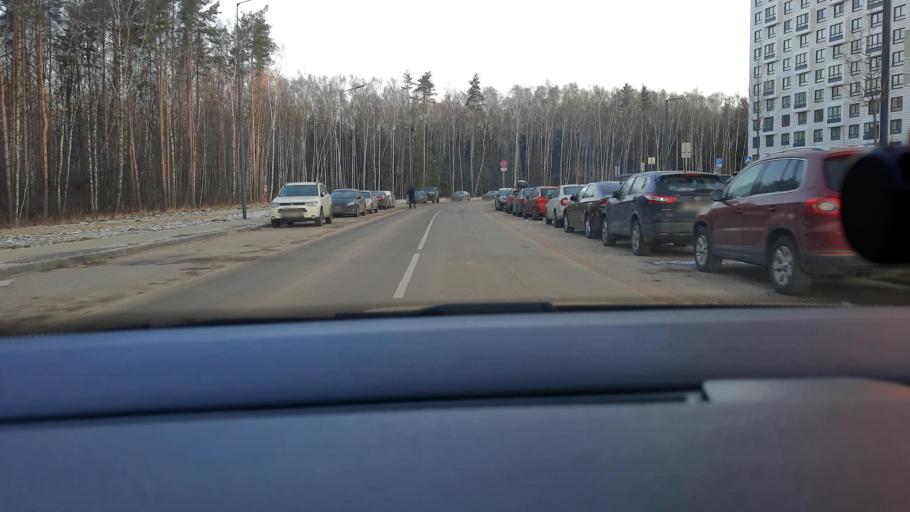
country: RU
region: Moscow
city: Solntsevo
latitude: 55.6181
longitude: 37.4067
